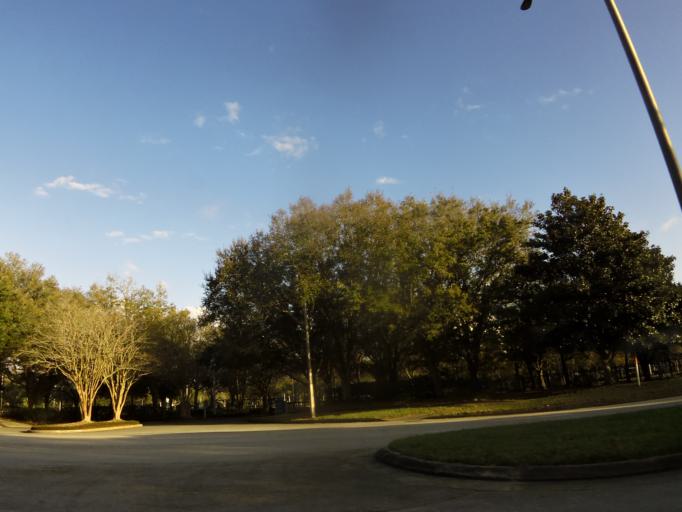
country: US
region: Florida
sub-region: Duval County
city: Jacksonville
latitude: 30.2578
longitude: -81.5471
